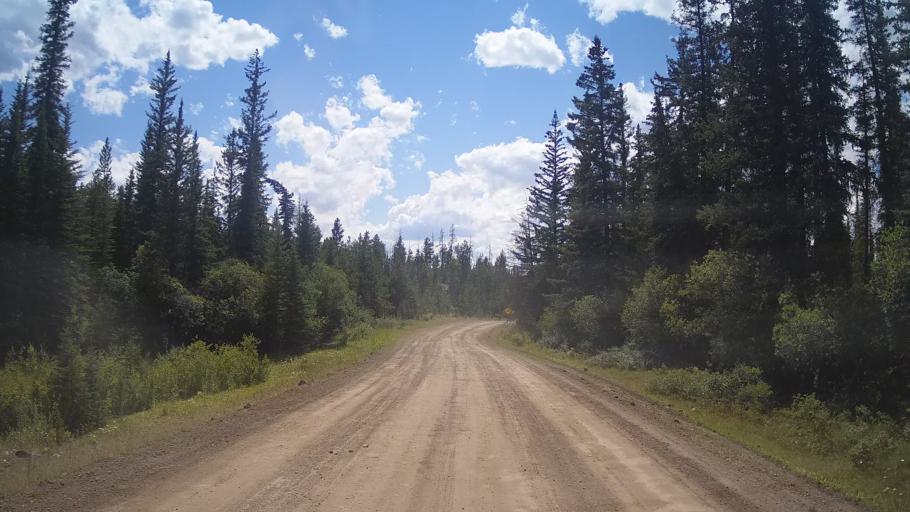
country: CA
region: British Columbia
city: Lillooet
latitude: 51.3389
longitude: -121.9541
